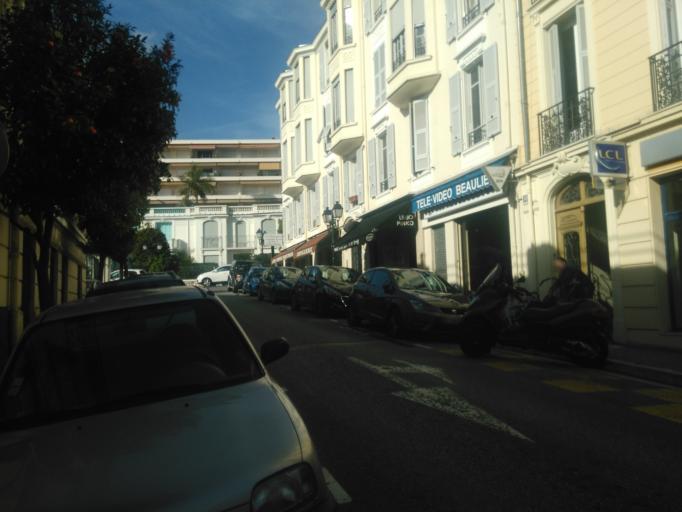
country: FR
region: Provence-Alpes-Cote d'Azur
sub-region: Departement des Alpes-Maritimes
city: Beaulieu-sur-Mer
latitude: 43.7072
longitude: 7.3305
